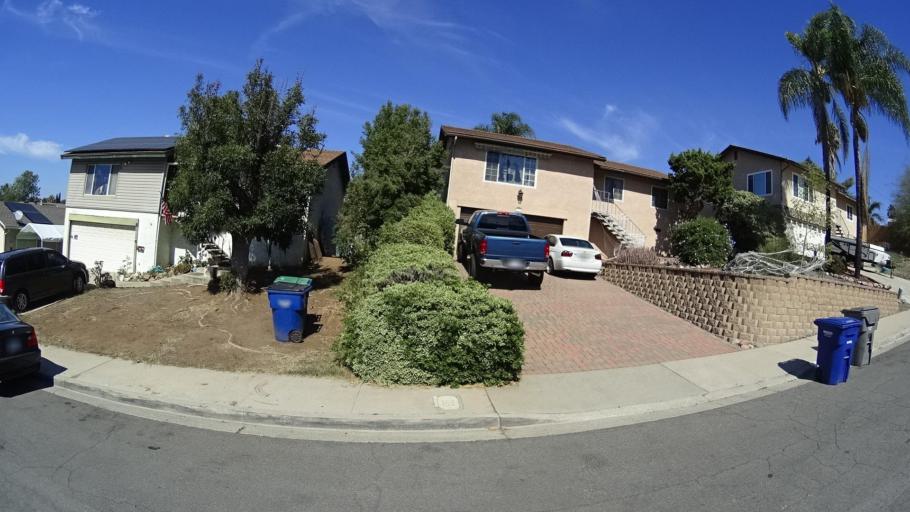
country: US
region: California
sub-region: San Diego County
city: La Presa
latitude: 32.7174
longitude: -117.0110
